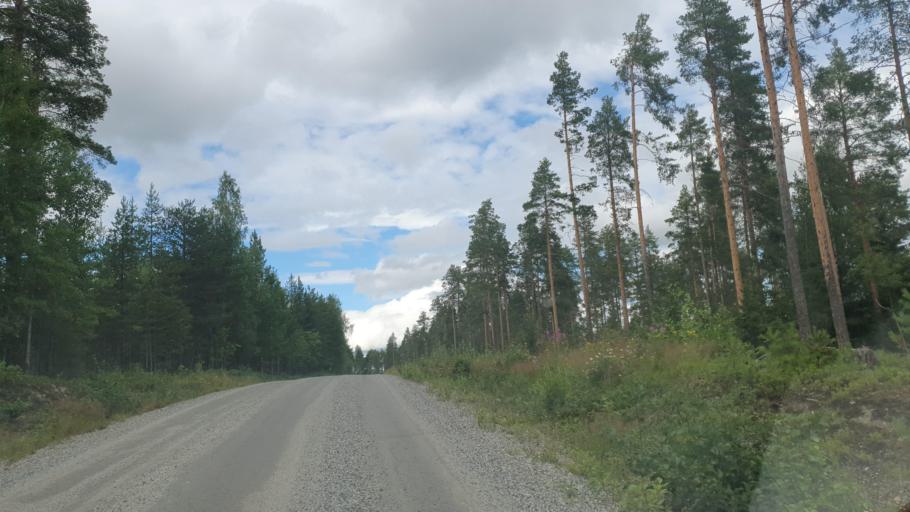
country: FI
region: Kainuu
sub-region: Kehys-Kainuu
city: Kuhmo
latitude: 64.0957
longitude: 29.4153
